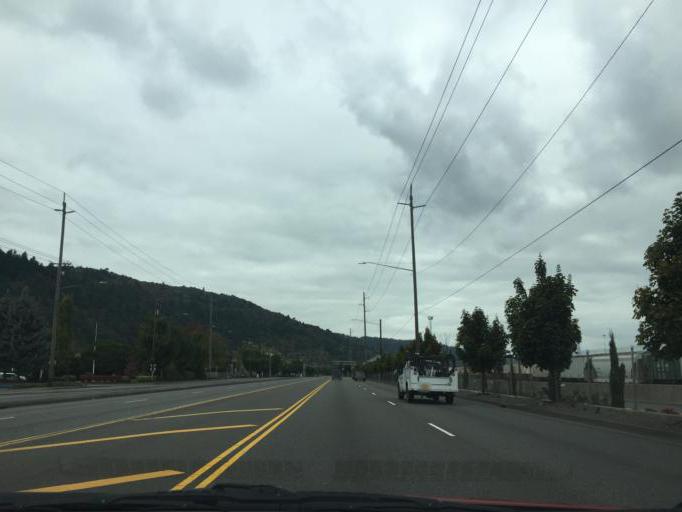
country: US
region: Oregon
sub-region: Multnomah County
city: Portland
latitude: 45.5497
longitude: -122.7196
